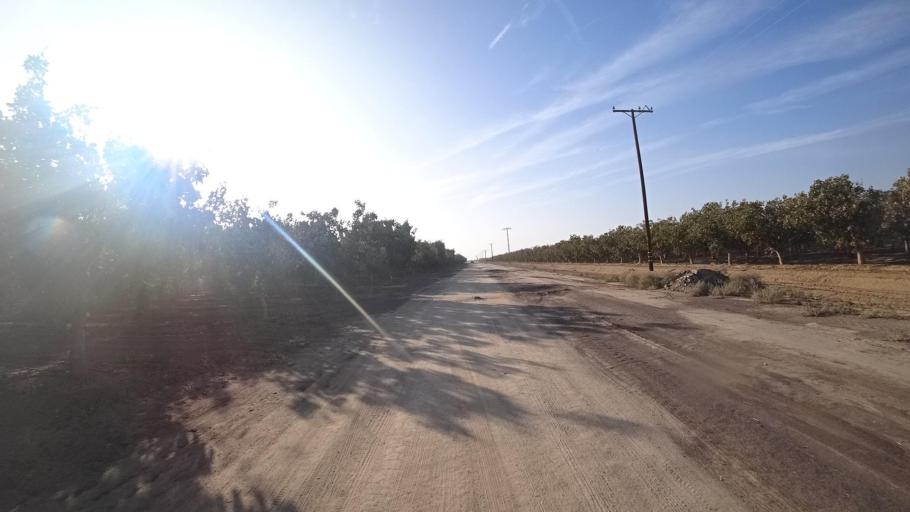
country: US
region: California
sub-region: Kern County
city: McFarland
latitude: 35.7210
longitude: -119.1872
